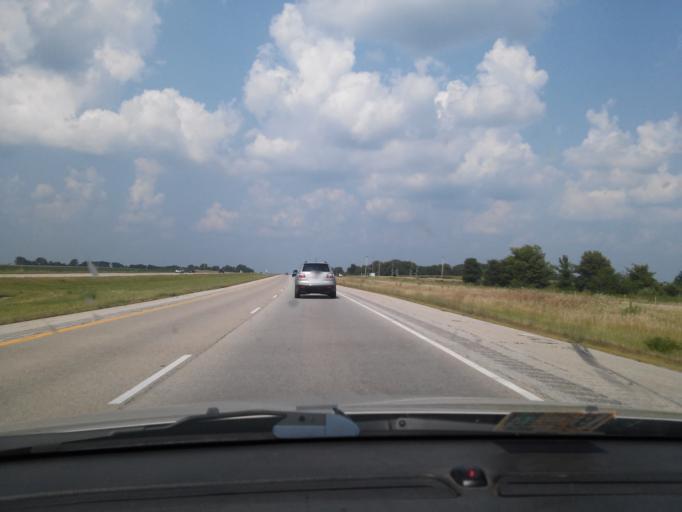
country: US
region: Illinois
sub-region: McLean County
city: Lexington
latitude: 40.5911
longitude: -88.8589
